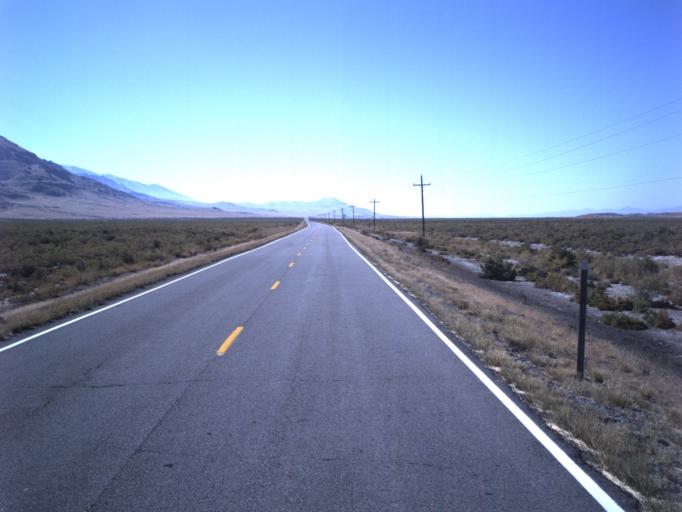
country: US
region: Utah
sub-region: Tooele County
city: Grantsville
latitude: 40.7360
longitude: -112.6559
